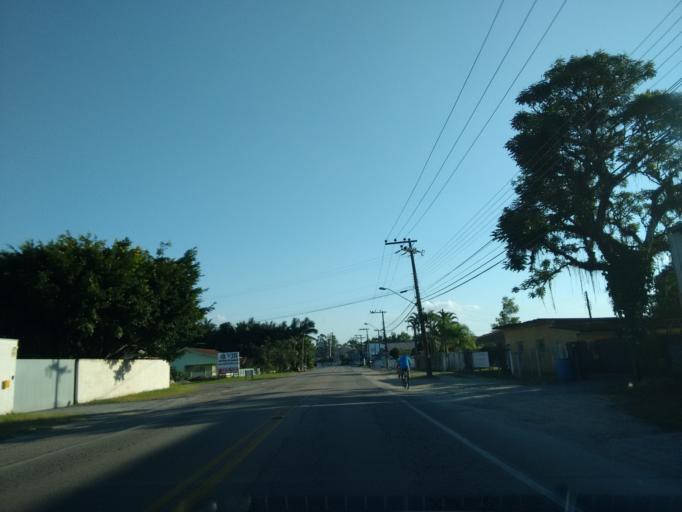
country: BR
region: Santa Catarina
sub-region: Gaspar
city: Gaspar
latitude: -26.9160
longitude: -48.9449
